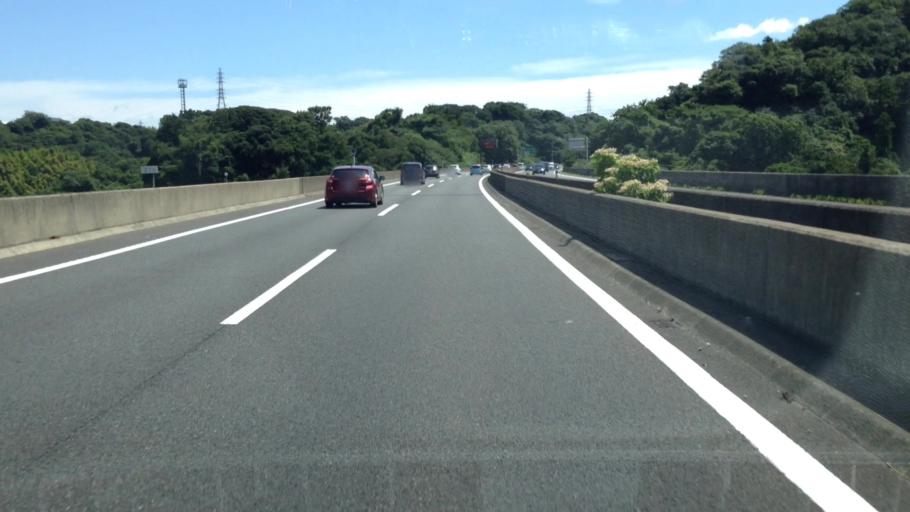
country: JP
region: Kanagawa
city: Yokosuka
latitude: 35.2818
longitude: 139.6284
